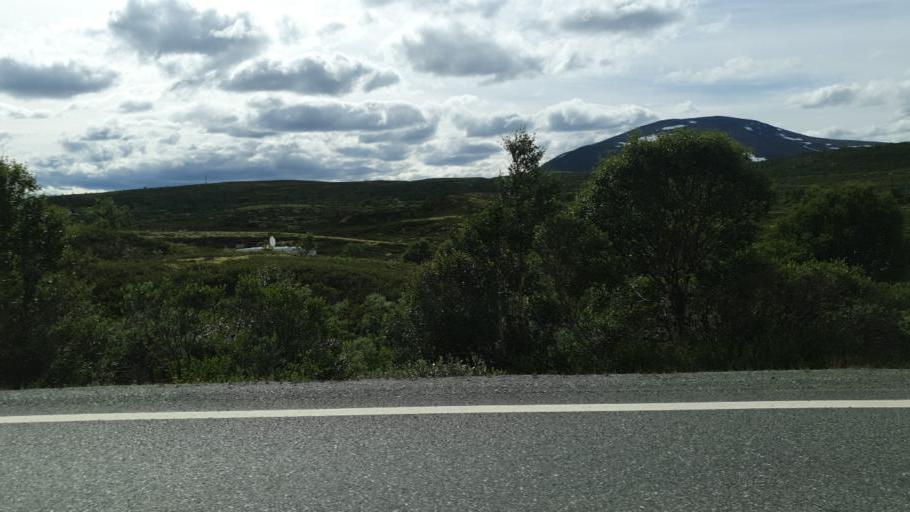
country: NO
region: Sor-Trondelag
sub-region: Oppdal
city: Oppdal
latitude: 62.2817
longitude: 9.5997
